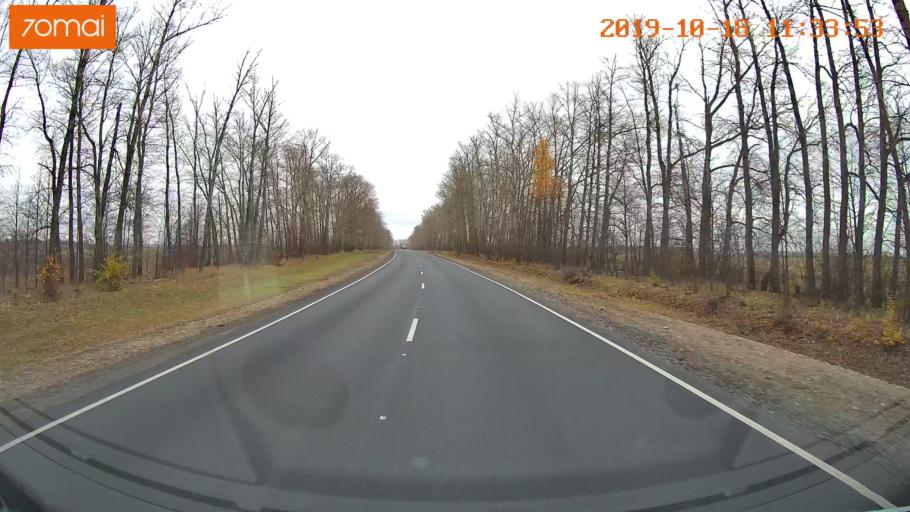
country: RU
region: Rjazan
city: Oktyabr'skiy
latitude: 54.1377
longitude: 38.7511
